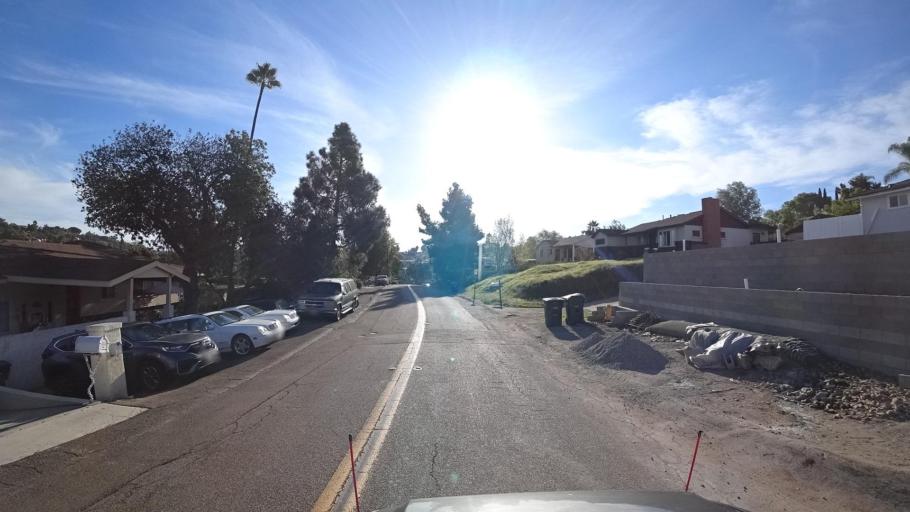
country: US
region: California
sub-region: San Diego County
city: Casa de Oro-Mount Helix
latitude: 32.7427
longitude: -116.9747
